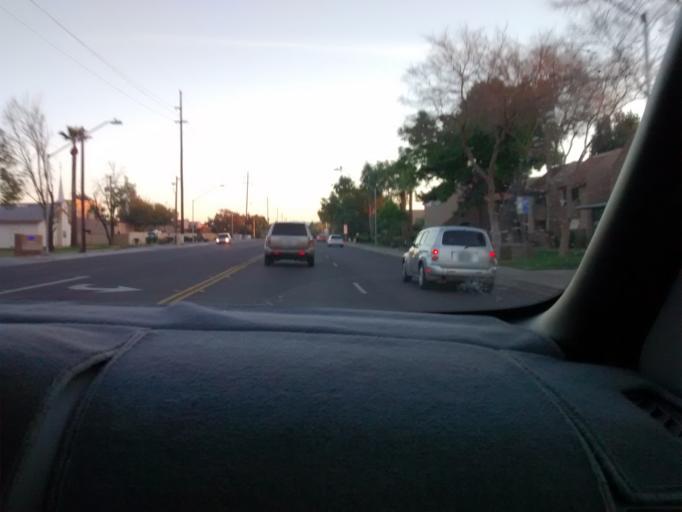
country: US
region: Arizona
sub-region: Maricopa County
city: Glendale
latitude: 33.5309
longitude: -112.2032
